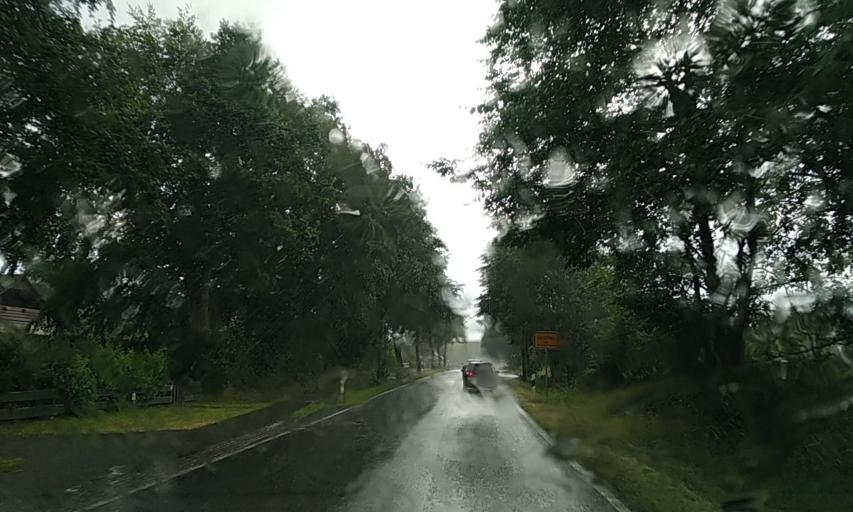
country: DE
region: Schleswig-Holstein
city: Lurschau
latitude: 54.5445
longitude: 9.4953
